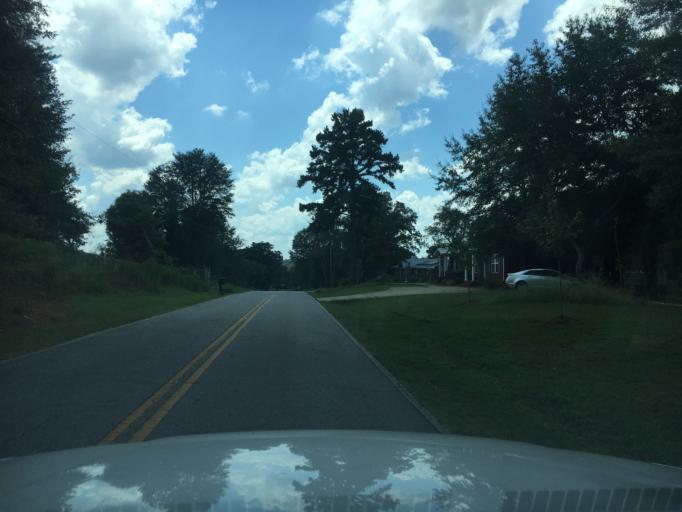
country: US
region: South Carolina
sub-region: Spartanburg County
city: Fairforest
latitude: 34.9034
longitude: -82.0527
